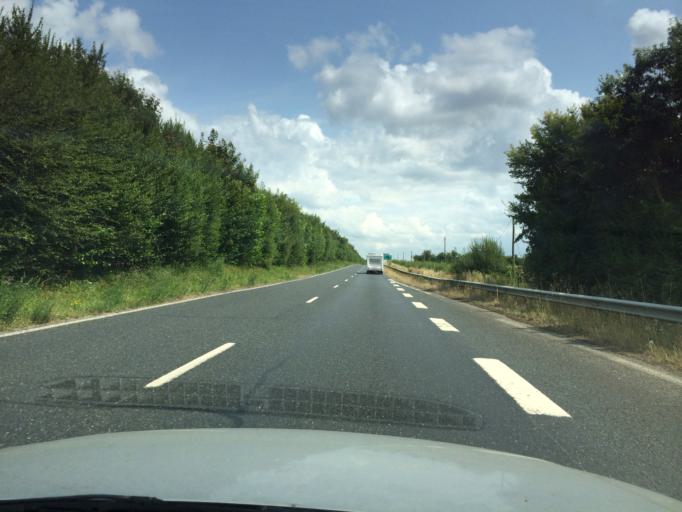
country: FR
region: Lower Normandy
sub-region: Departement du Calvados
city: Grandcamp-Maisy
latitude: 49.3389
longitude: -0.9402
